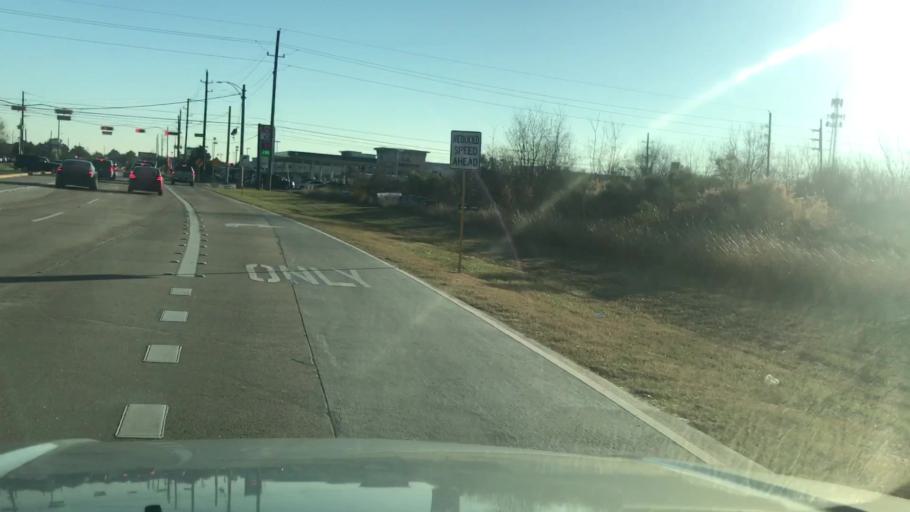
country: US
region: Texas
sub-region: Fort Bend County
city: Cinco Ranch
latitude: 29.8321
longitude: -95.7201
